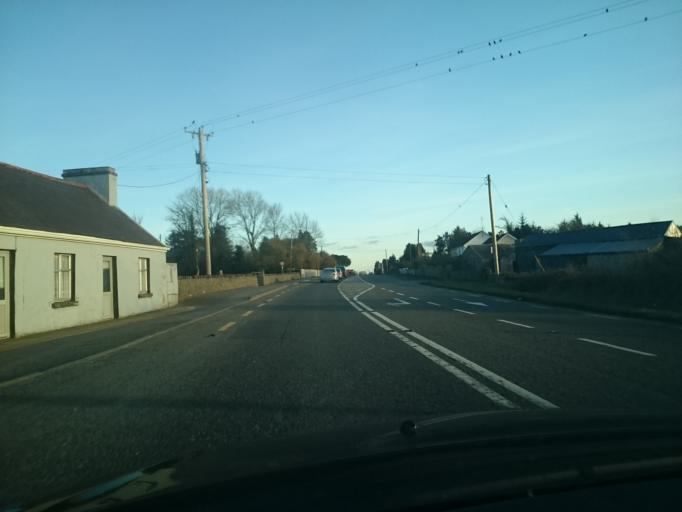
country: IE
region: Connaught
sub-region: Maigh Eo
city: Claremorris
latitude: 53.7368
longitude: -9.0076
